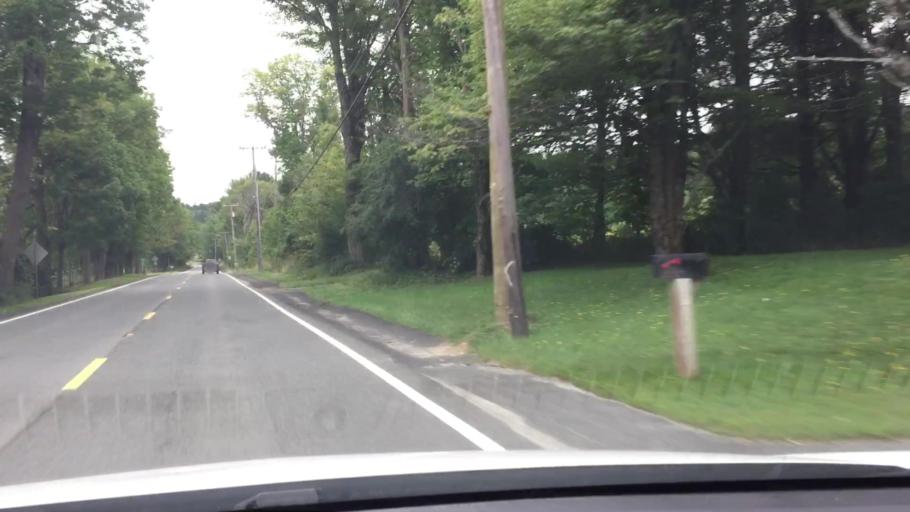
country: US
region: Massachusetts
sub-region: Berkshire County
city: Hinsdale
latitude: 42.3949
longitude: -73.1248
